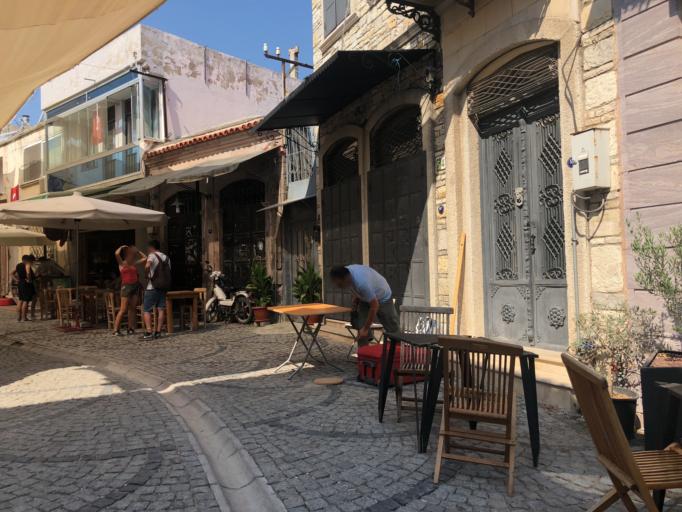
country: TR
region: Izmir
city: Urla
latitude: 38.3221
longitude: 26.7650
